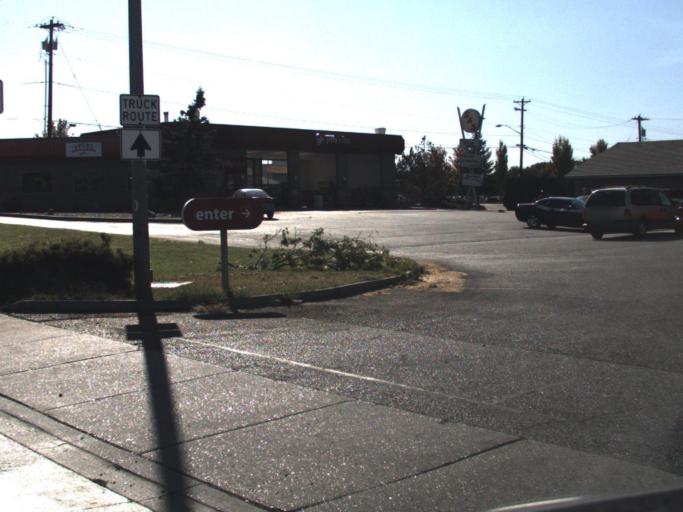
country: US
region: Washington
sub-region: Benton County
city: Kennewick
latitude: 46.1992
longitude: -119.1592
